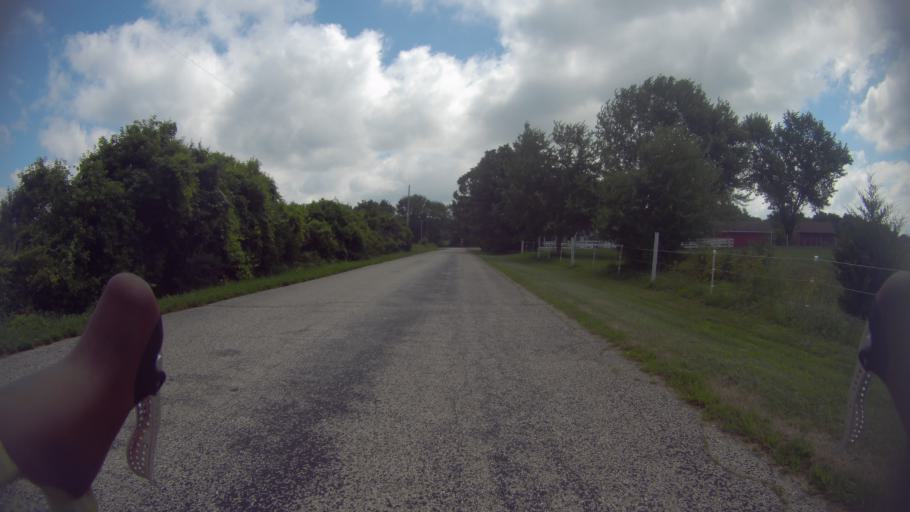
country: US
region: Wisconsin
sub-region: Columbia County
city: Lodi
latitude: 43.2298
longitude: -89.5980
